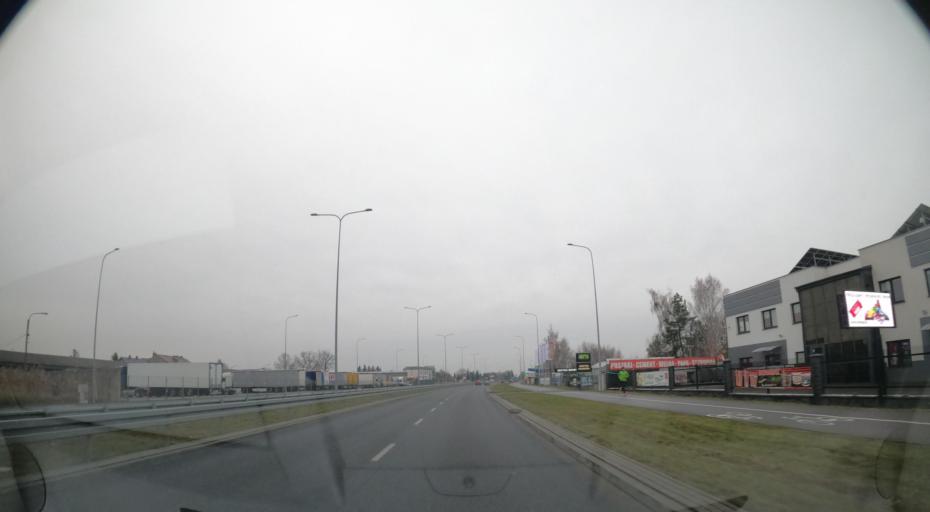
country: PL
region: Masovian Voivodeship
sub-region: Radom
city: Radom
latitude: 51.3907
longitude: 21.1940
